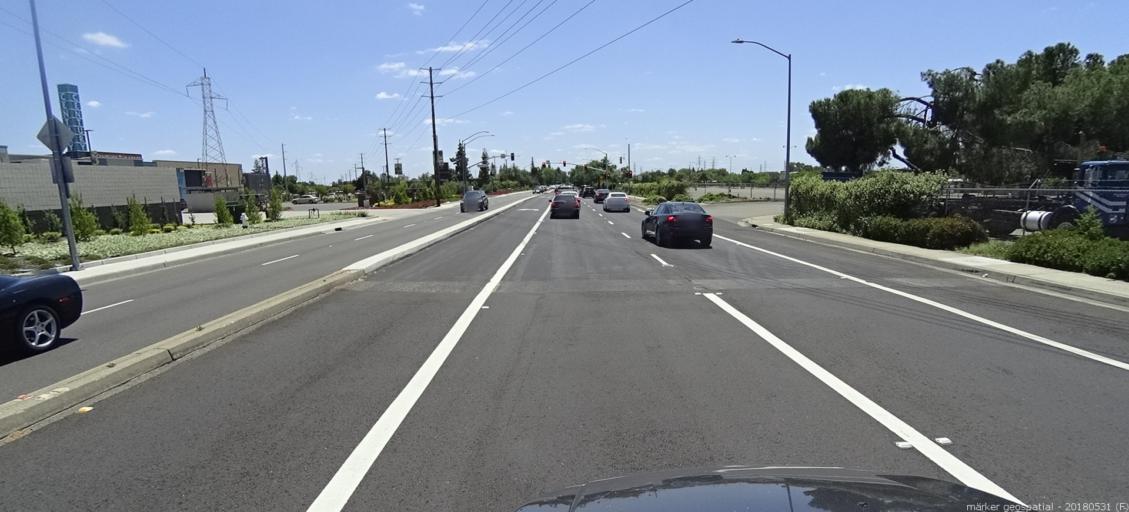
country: US
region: California
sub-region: Sacramento County
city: Arden-Arcade
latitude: 38.5947
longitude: -121.4201
